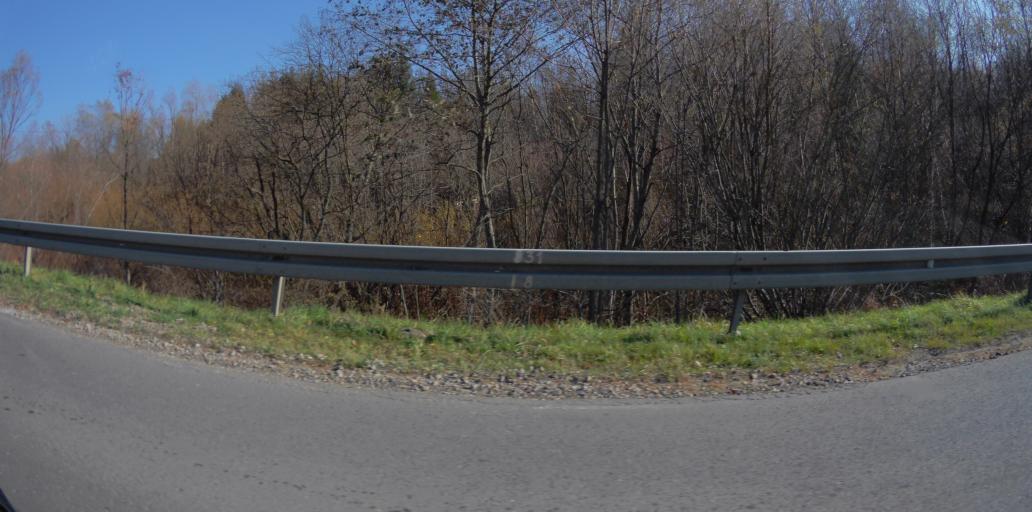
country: PL
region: Subcarpathian Voivodeship
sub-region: Powiat bieszczadzki
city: Lutowiska
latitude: 49.2015
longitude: 22.6753
